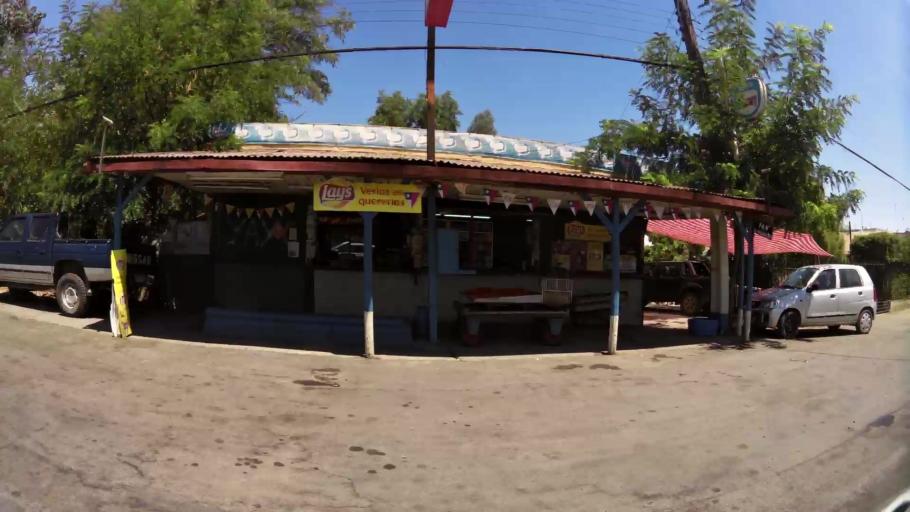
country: CL
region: Maule
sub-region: Provincia de Curico
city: Curico
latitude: -34.9848
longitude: -71.2150
